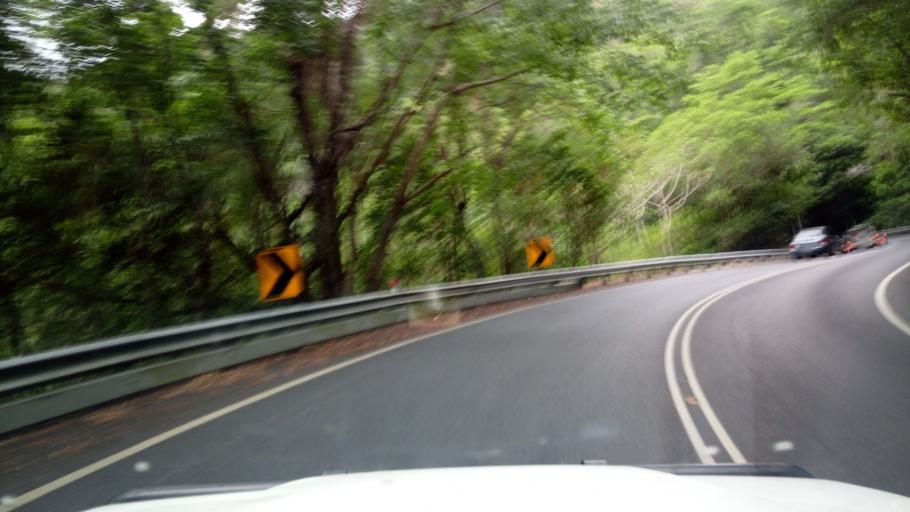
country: AU
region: Queensland
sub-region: Cairns
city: Redlynch
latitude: -16.8432
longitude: 145.6805
